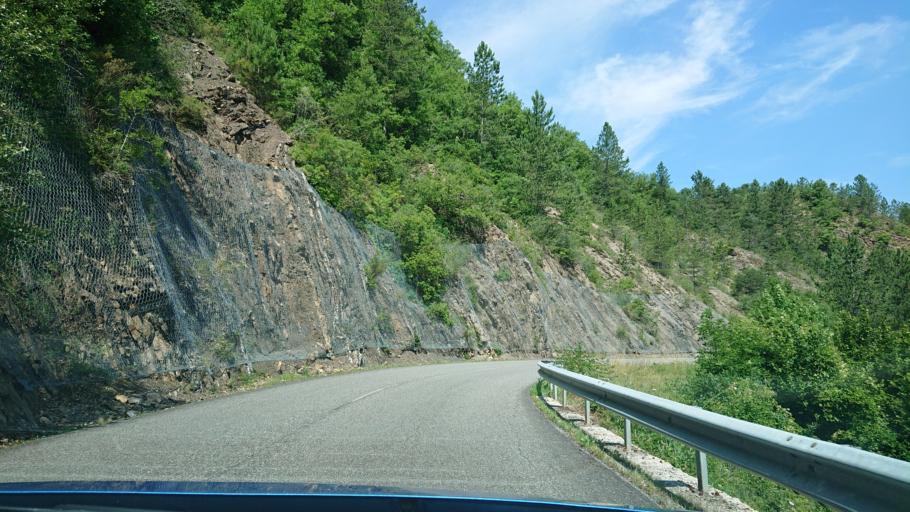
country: FR
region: Provence-Alpes-Cote d'Azur
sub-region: Departement des Alpes-de-Haute-Provence
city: Sisteron
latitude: 44.2746
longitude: 6.0108
